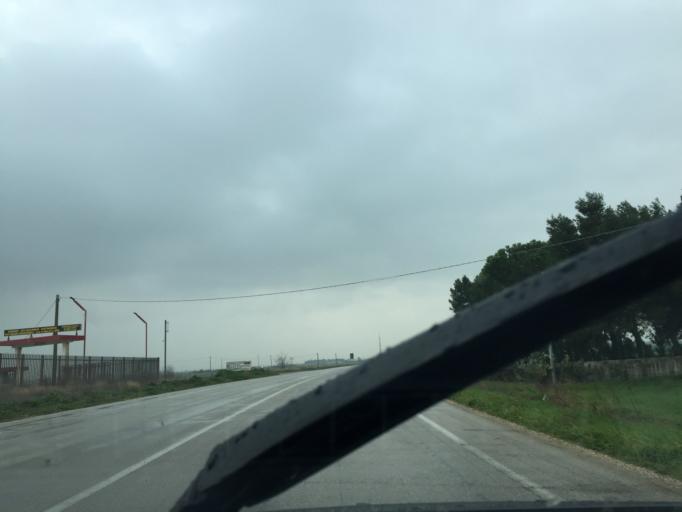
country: IT
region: Apulia
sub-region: Provincia di Foggia
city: Foggia
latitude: 41.4859
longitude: 15.5218
